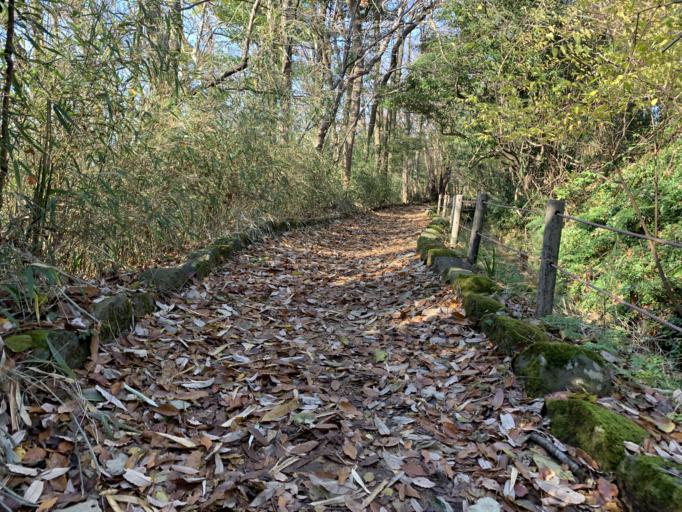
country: JP
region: Ishikawa
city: Nonoichi
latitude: 36.5390
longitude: 136.6864
